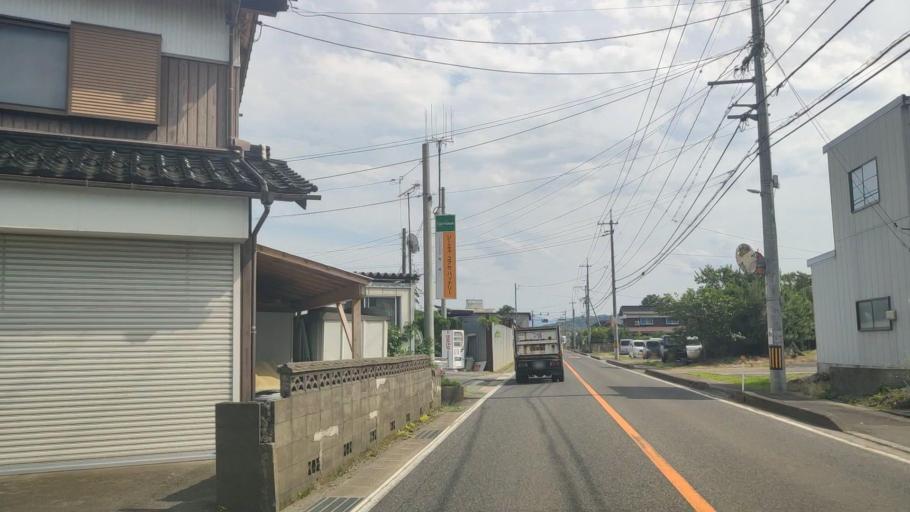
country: JP
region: Tottori
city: Tottori
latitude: 35.4680
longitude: 134.2039
